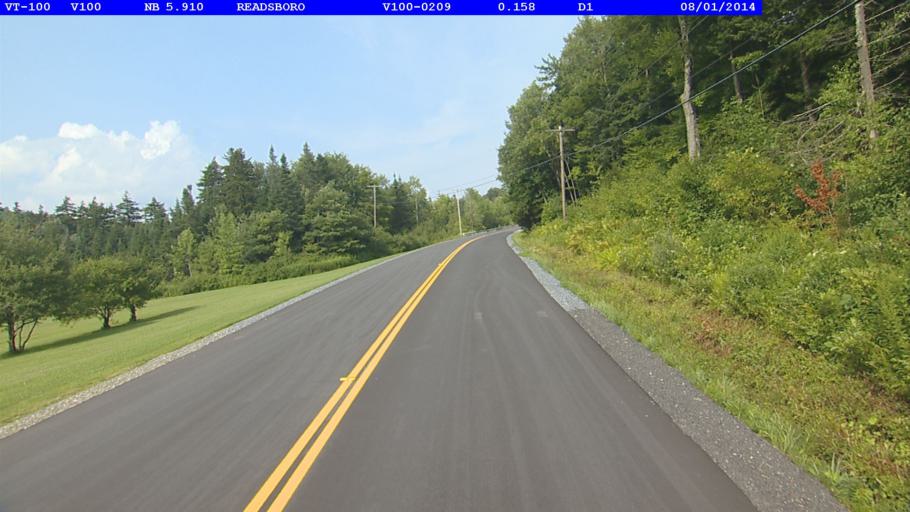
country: US
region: Massachusetts
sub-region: Berkshire County
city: North Adams
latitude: 42.8111
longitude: -73.0139
